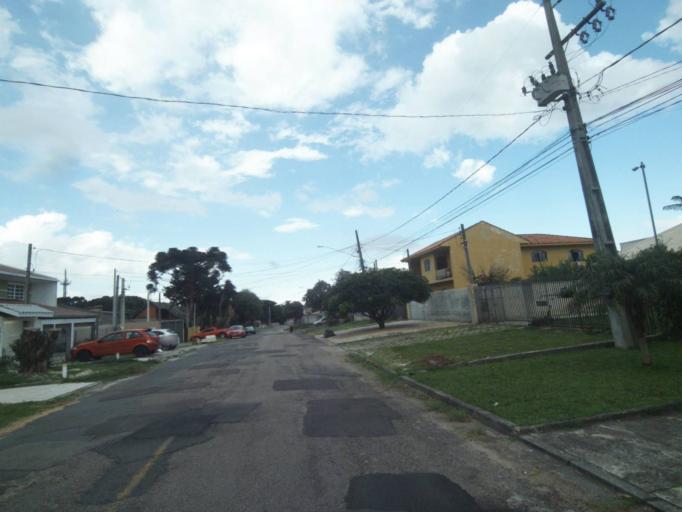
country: BR
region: Parana
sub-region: Pinhais
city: Pinhais
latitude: -25.4463
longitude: -49.2105
